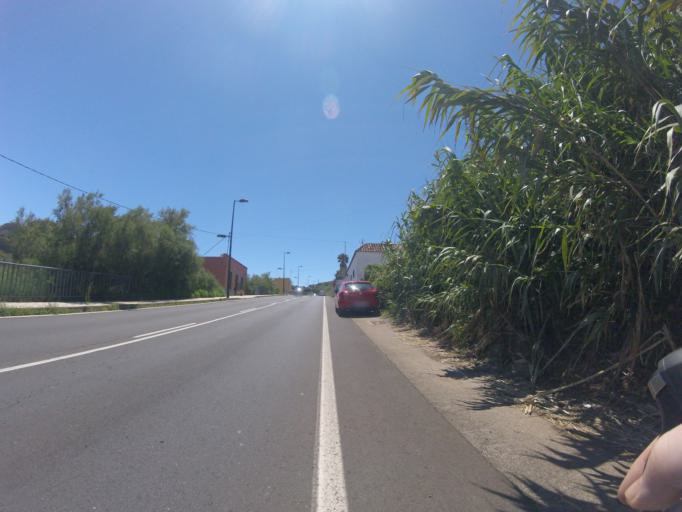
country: ES
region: Canary Islands
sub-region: Provincia de Santa Cruz de Tenerife
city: Tegueste
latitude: 28.5155
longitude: -16.3171
